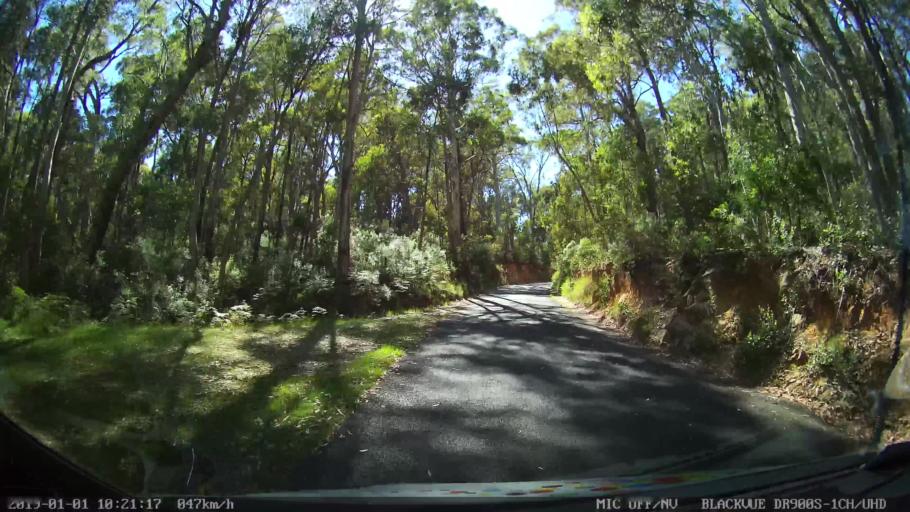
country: AU
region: New South Wales
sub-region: Snowy River
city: Jindabyne
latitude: -36.0756
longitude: 148.1943
